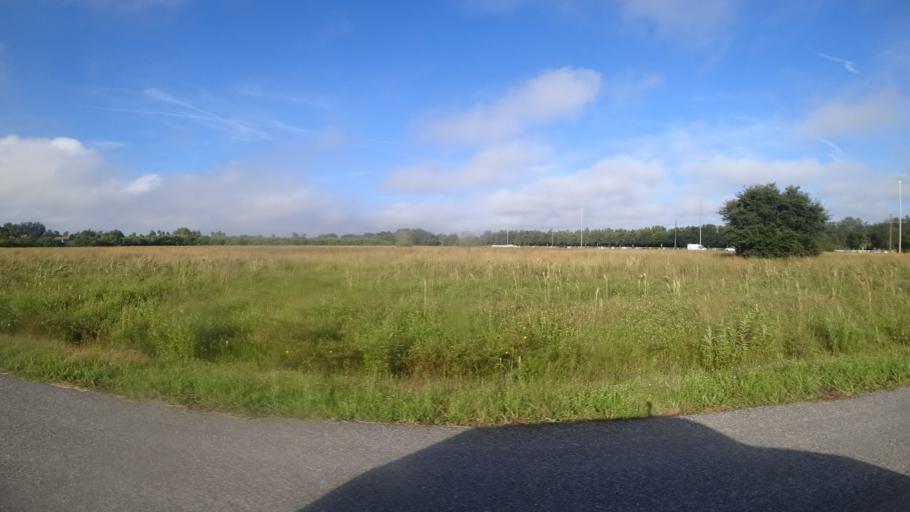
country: US
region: Florida
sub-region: Manatee County
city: Ellenton
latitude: 27.5469
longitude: -82.4664
